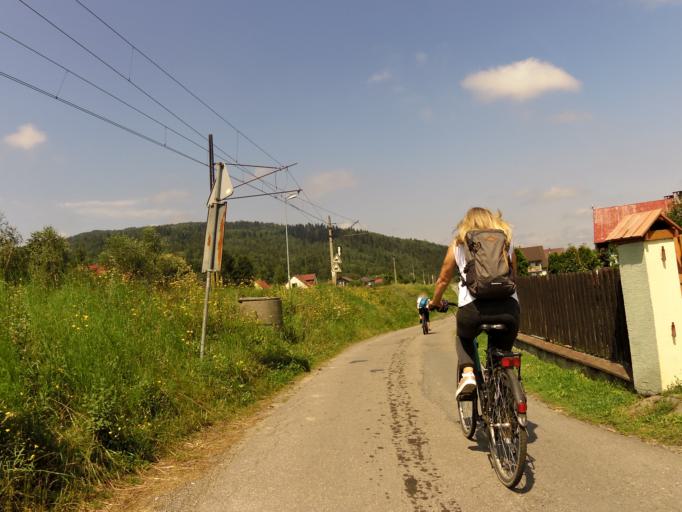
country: PL
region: Silesian Voivodeship
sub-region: Powiat zywiecki
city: Rajcza
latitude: 49.5194
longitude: 19.1103
